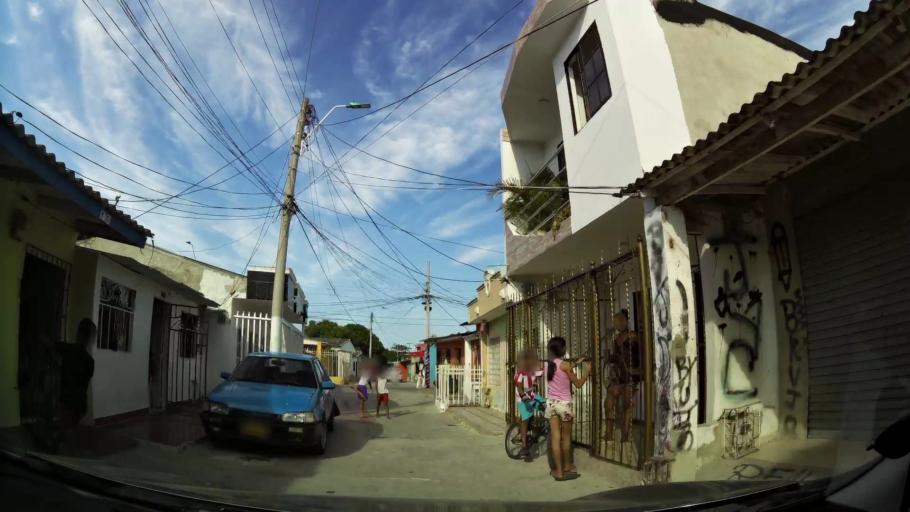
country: CO
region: Atlantico
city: Soledad
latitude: 10.9243
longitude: -74.8121
